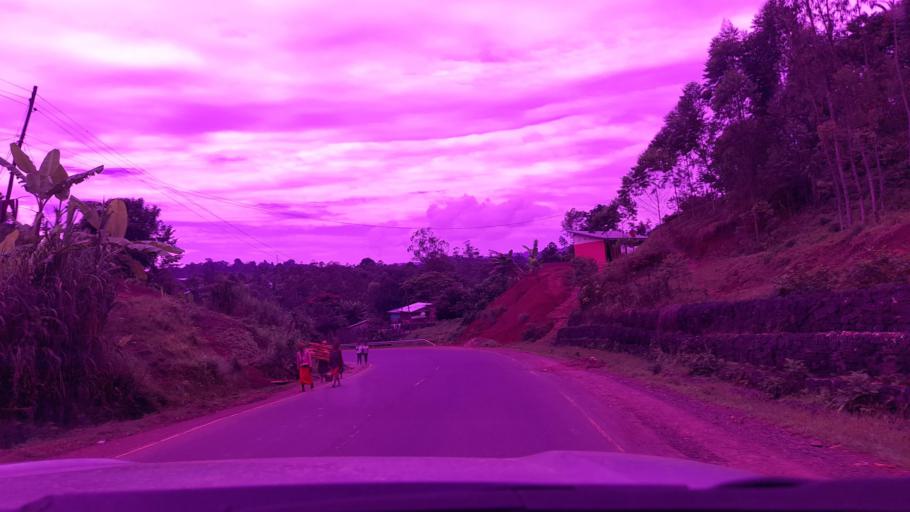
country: ET
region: Southern Nations, Nationalities, and People's Region
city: Mizan Teferi
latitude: 7.0031
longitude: 35.6013
